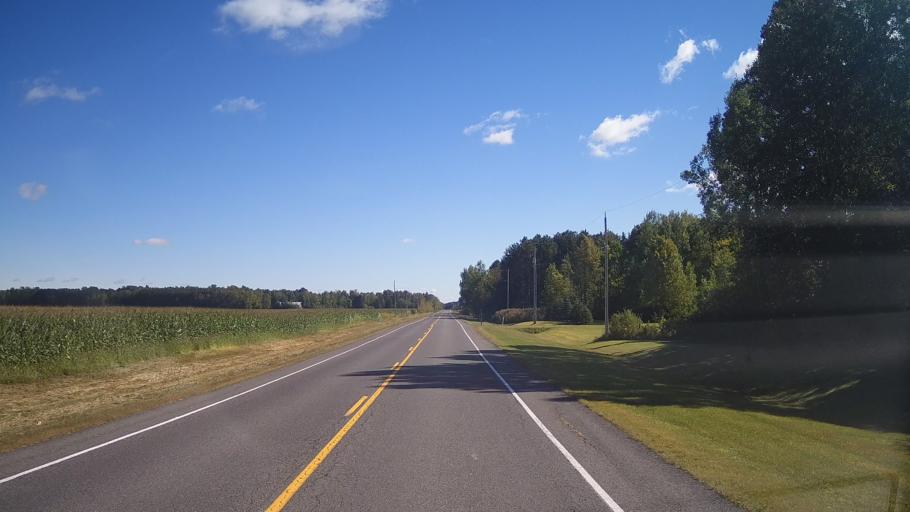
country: CA
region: Ontario
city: Prescott
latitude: 44.9097
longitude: -75.4302
